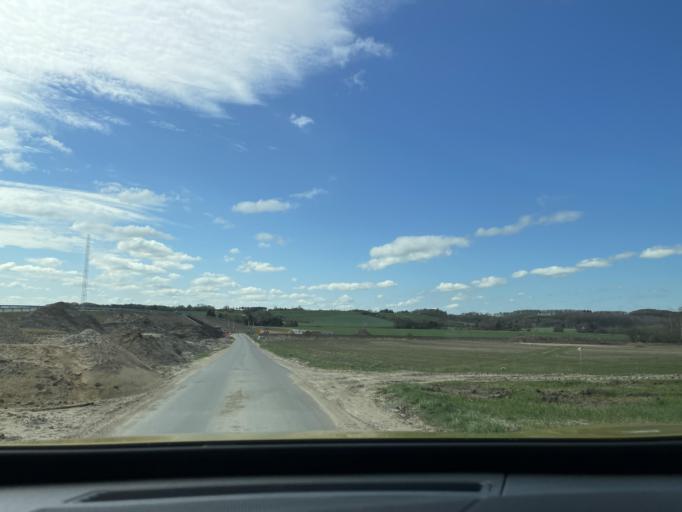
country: DK
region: Central Jutland
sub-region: Favrskov Kommune
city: Hinnerup
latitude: 56.2944
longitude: 10.0972
